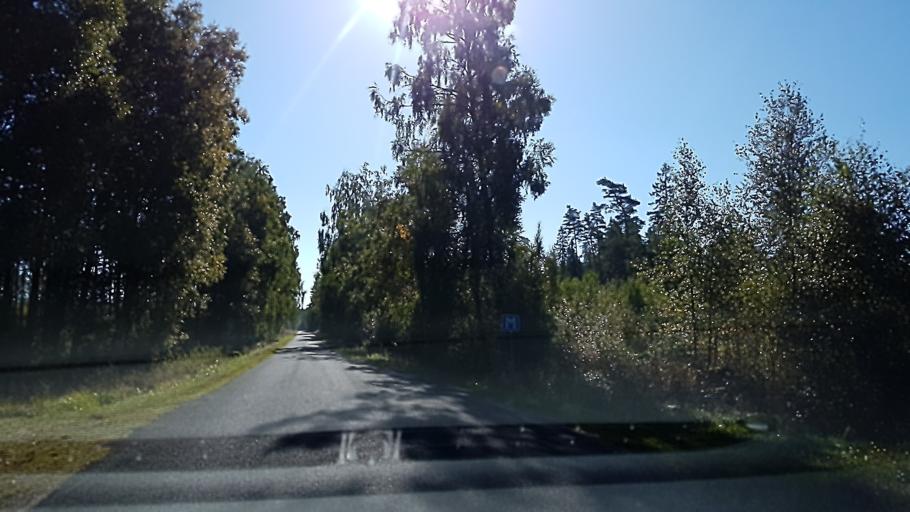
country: SE
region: Kronoberg
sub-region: Ljungby Kommun
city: Ljungby
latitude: 56.8073
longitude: 14.0249
